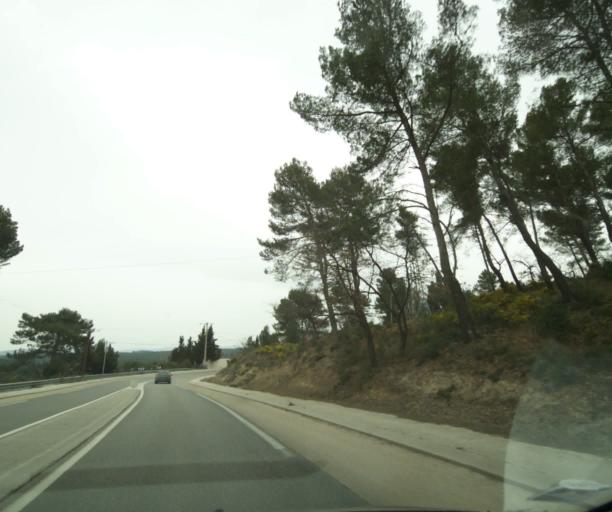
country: FR
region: Provence-Alpes-Cote d'Azur
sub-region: Departement des Bouches-du-Rhone
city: Fuveau
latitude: 43.4521
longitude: 5.5459
